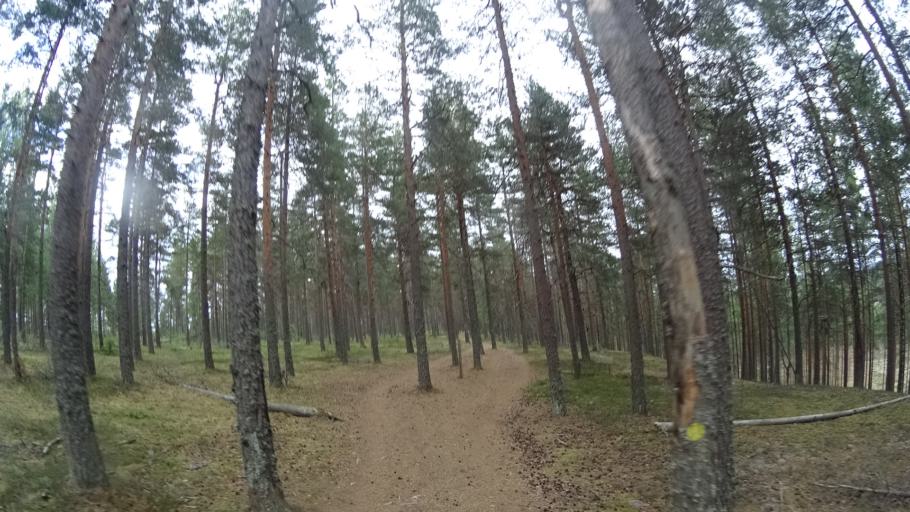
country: FI
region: Satakunta
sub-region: Pohjois-Satakunta
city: Jaemijaervi
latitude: 61.7748
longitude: 22.7253
